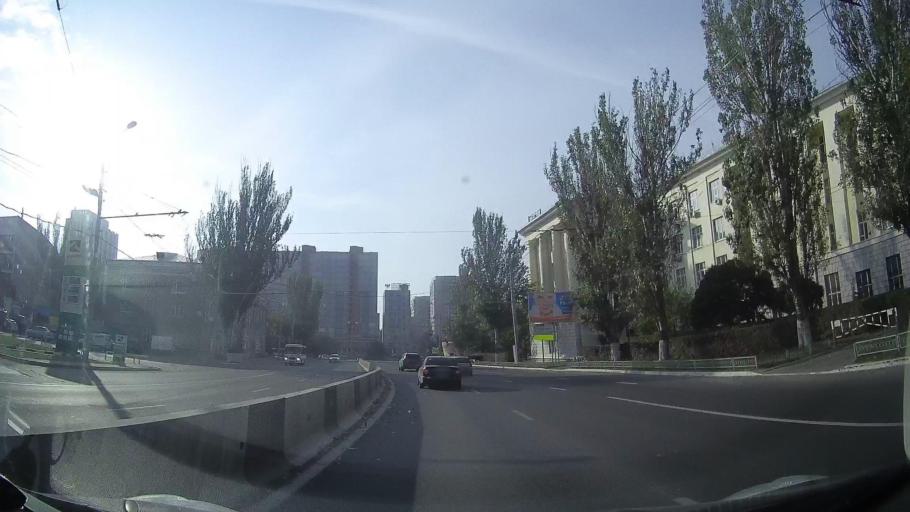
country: RU
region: Rostov
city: Rostov-na-Donu
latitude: 47.2377
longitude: 39.7136
